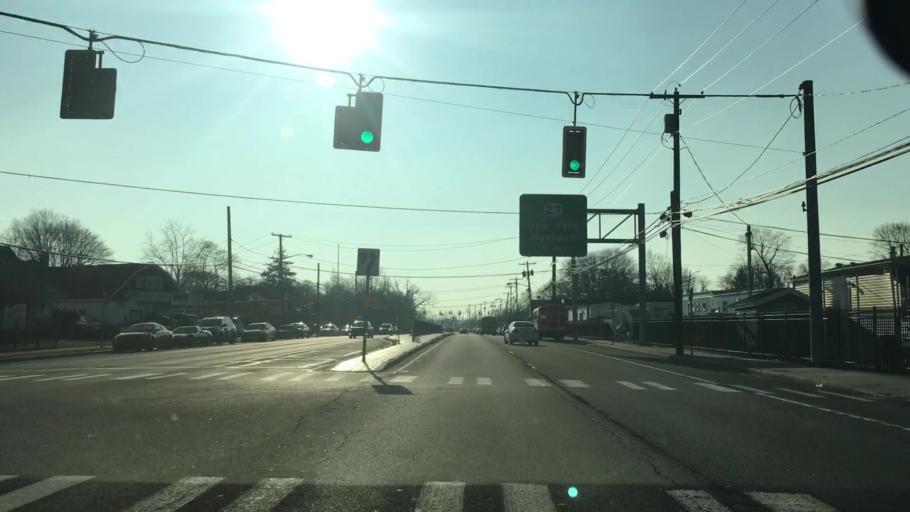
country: US
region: New York
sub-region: Suffolk County
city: North Amityville
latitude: 40.6942
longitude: -73.4235
